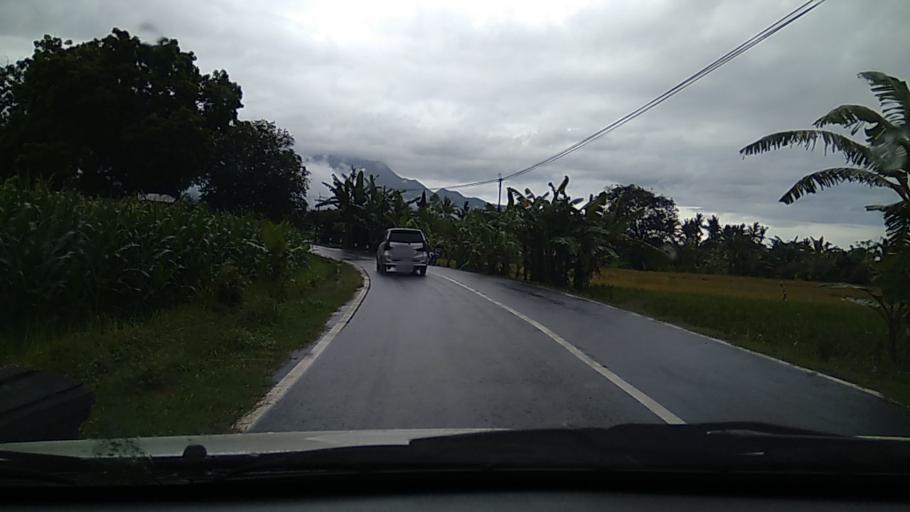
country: ID
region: Bali
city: Banjar Danginsema
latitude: -8.4649
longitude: 115.6220
